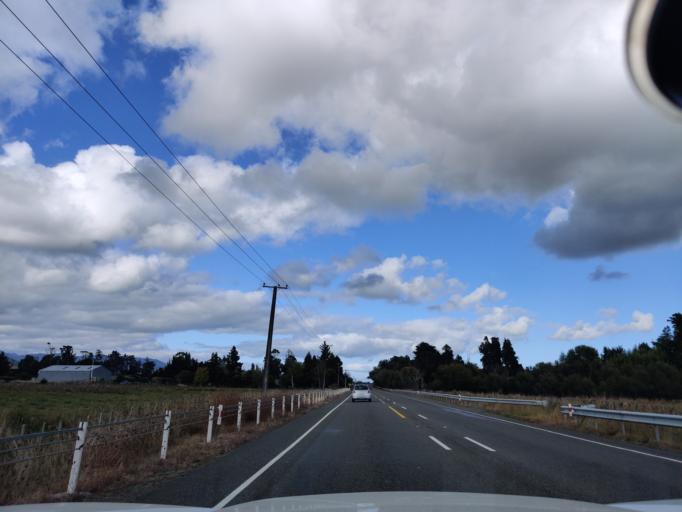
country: NZ
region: Manawatu-Wanganui
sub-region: Horowhenua District
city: Levin
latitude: -40.6020
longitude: 175.3345
